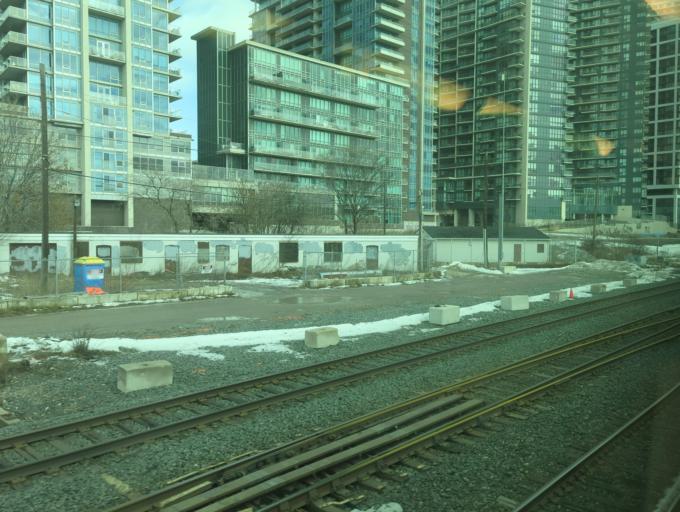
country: CA
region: Ontario
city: Toronto
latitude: 43.6375
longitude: -79.4136
